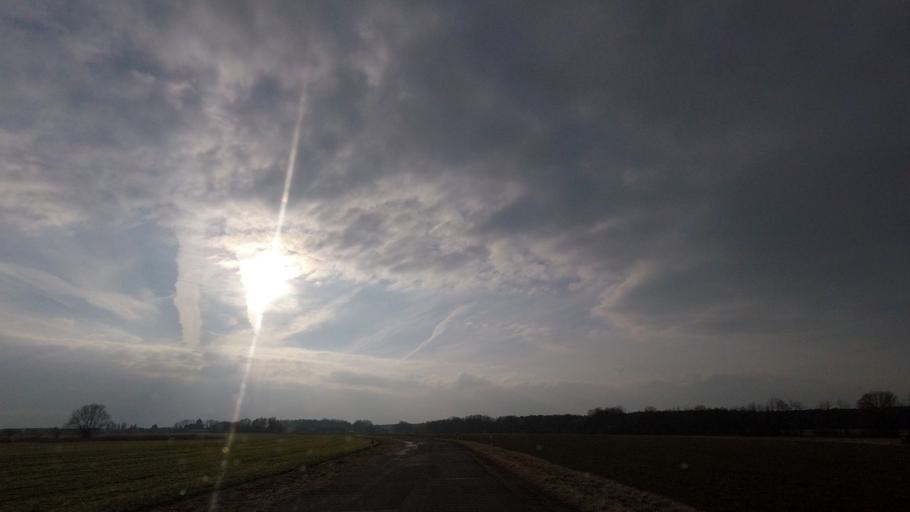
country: DE
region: Brandenburg
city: Belzig
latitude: 52.1549
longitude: 12.6644
